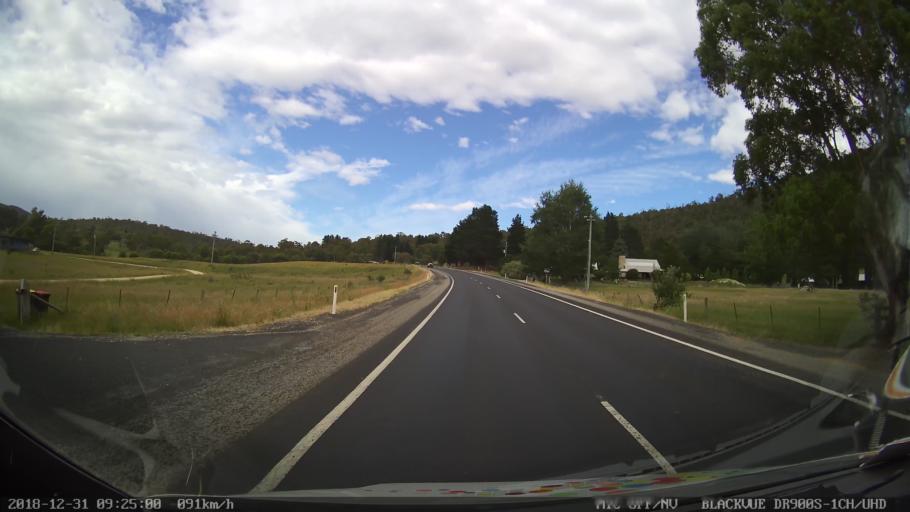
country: AU
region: New South Wales
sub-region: Snowy River
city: Jindabyne
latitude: -36.4409
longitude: 148.5130
